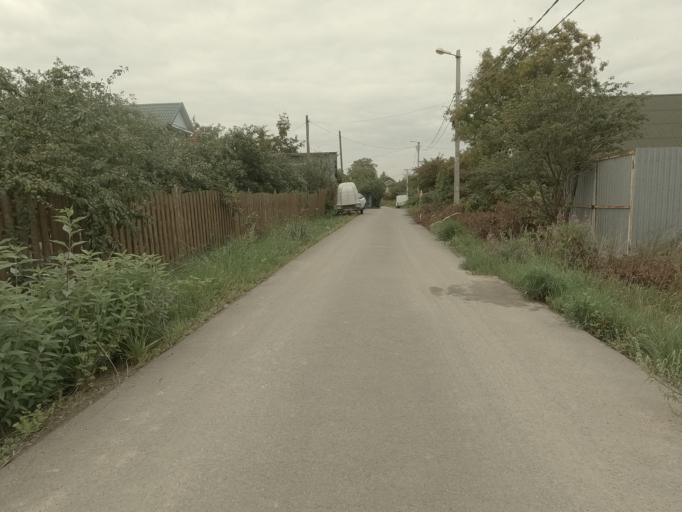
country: RU
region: Leningrad
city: Koltushi
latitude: 59.8968
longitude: 30.6711
